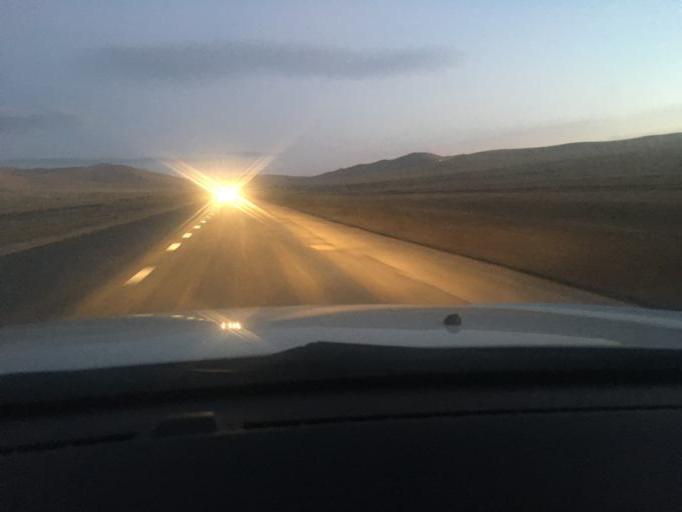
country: MN
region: Central Aimak
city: Altanbulag
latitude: 47.9920
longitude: 106.5570
